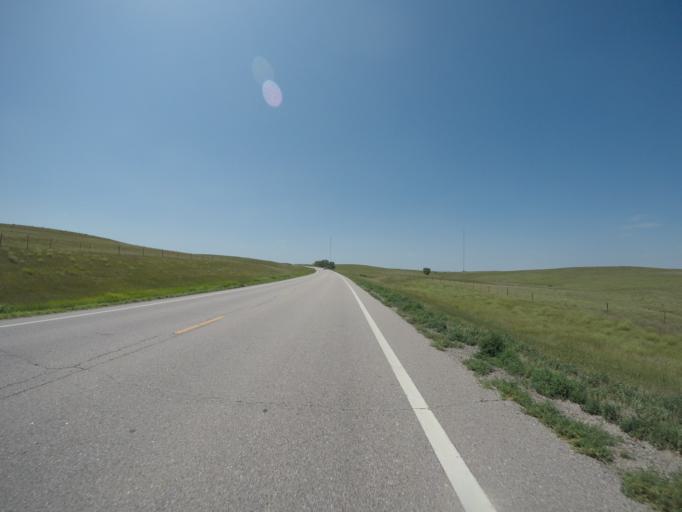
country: US
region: Kansas
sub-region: Osborne County
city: Osborne
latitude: 39.4889
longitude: -98.6967
